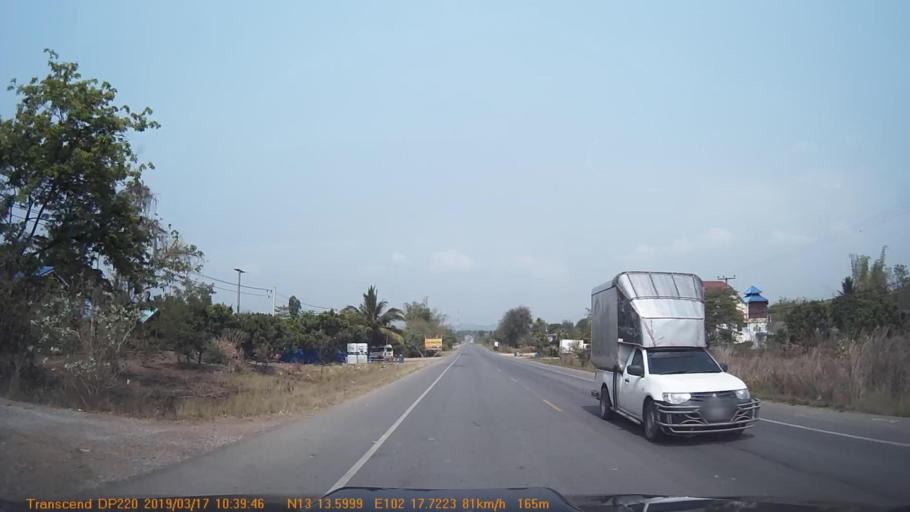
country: TH
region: Chanthaburi
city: Soi Dao
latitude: 13.2269
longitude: 102.2950
